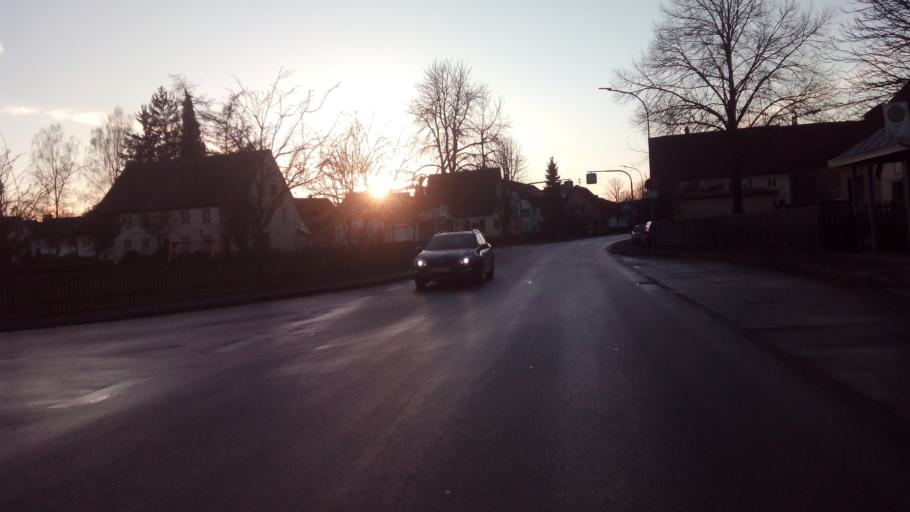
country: DE
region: Baden-Wuerttemberg
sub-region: Tuebingen Region
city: Erbach
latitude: 48.3300
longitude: 9.8537
